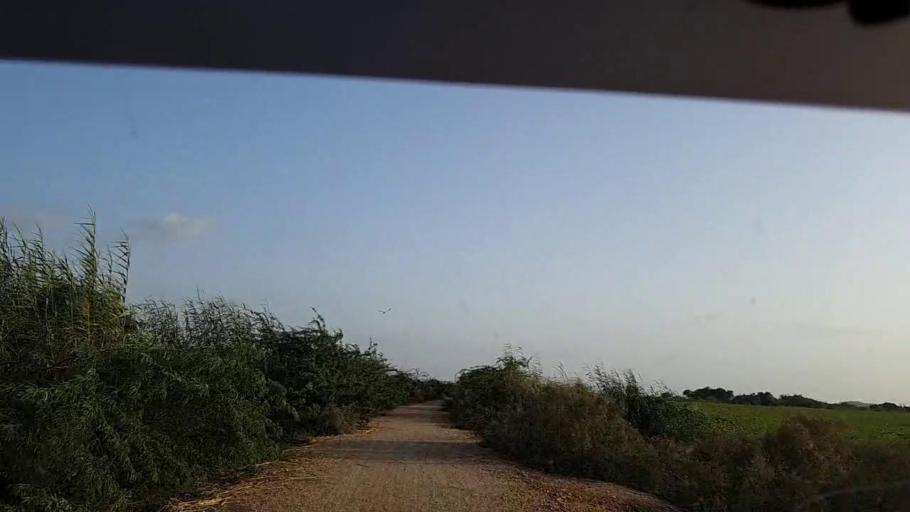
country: PK
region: Sindh
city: Kadhan
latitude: 24.5457
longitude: 68.9522
